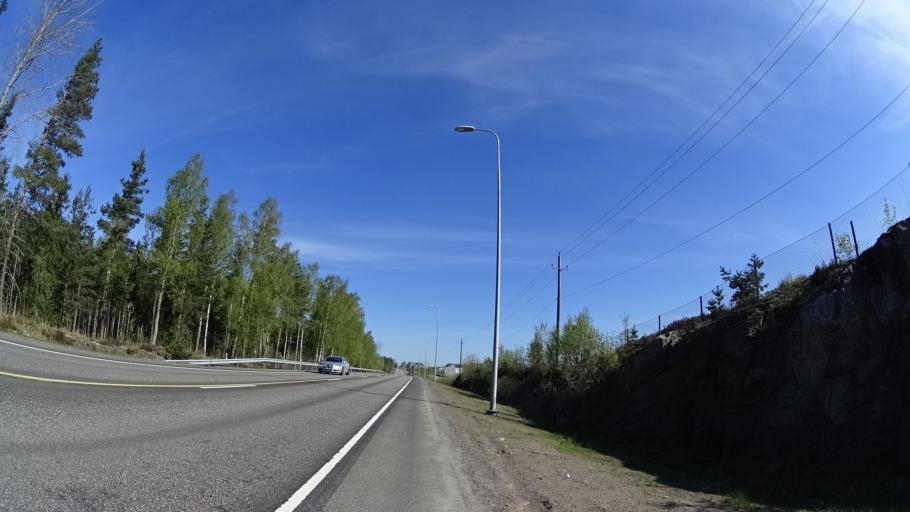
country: FI
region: Uusimaa
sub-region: Helsinki
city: Nurmijaervi
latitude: 60.4450
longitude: 24.8334
